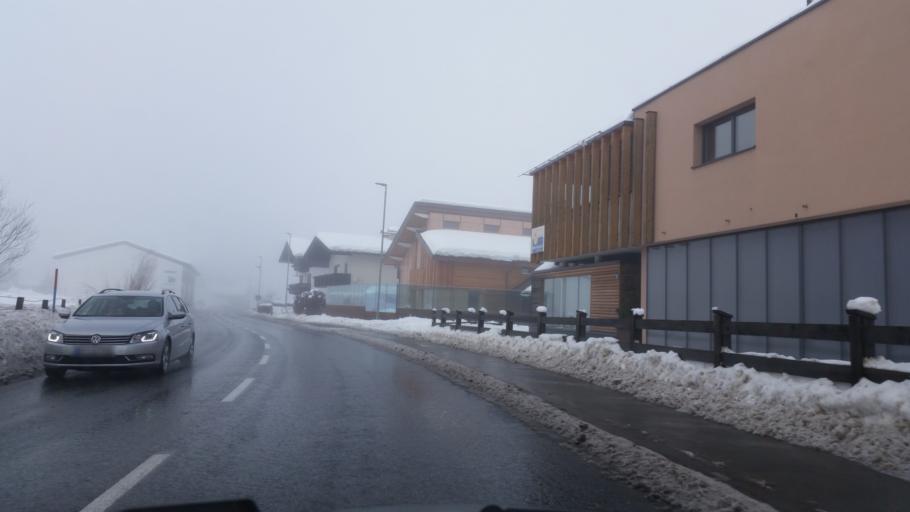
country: AT
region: Tyrol
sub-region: Politischer Bezirk Kitzbuhel
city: Sankt Johann in Tirol
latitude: 47.5202
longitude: 12.4366
